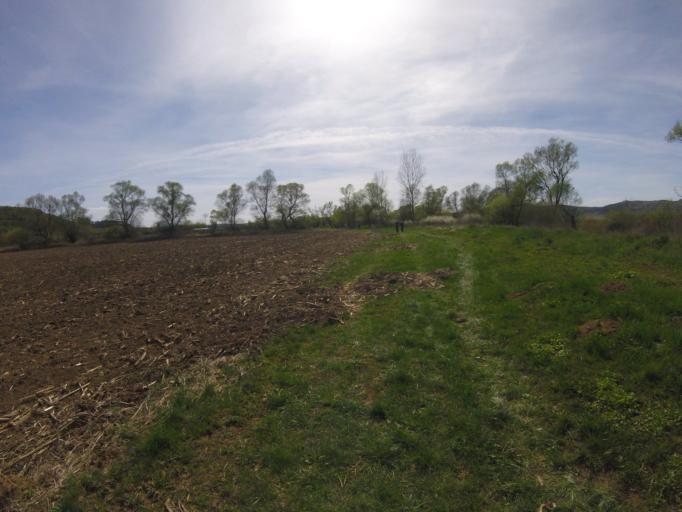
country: HU
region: Borsod-Abauj-Zemplen
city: Szendro
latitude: 48.4242
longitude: 20.7309
